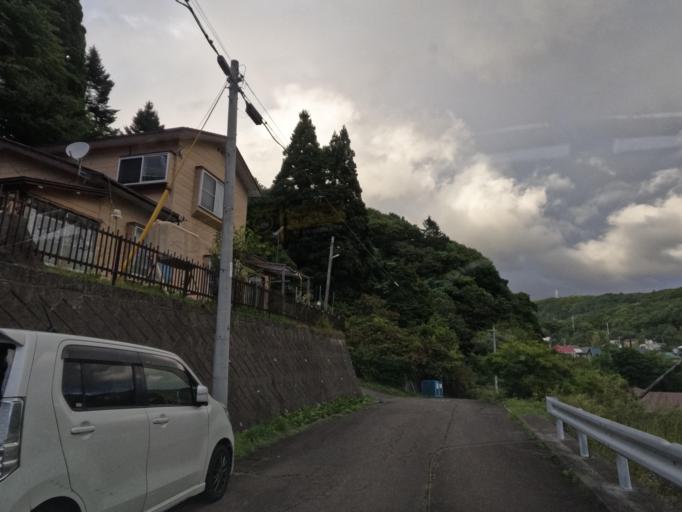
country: JP
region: Hokkaido
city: Muroran
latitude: 42.3711
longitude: 140.9535
